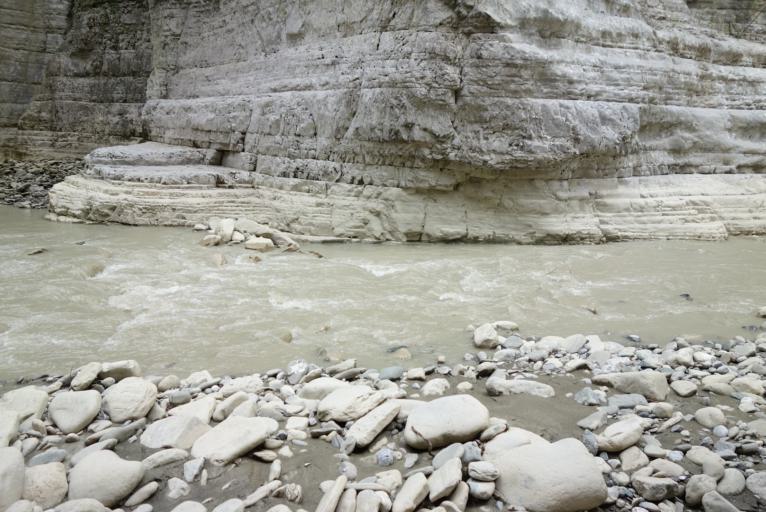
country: AL
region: Gjirokaster
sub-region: Rrethi i Permetit
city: Petran
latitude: 40.2541
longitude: 20.4532
